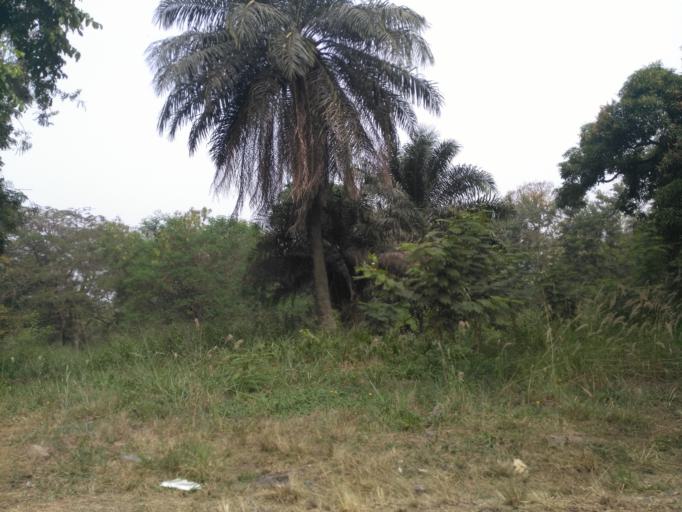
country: GH
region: Ashanti
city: Kumasi
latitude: 6.6805
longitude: -1.6230
